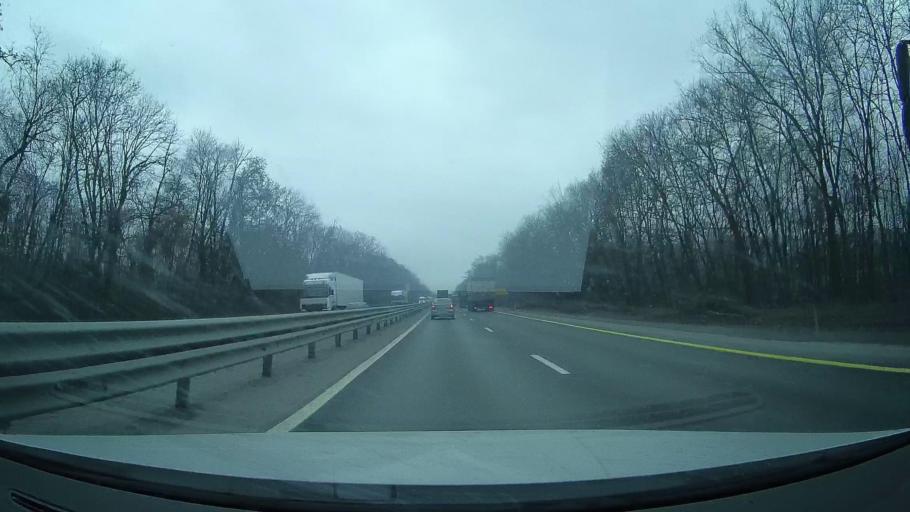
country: RU
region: Rostov
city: Aksay
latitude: 47.3139
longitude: 39.8633
